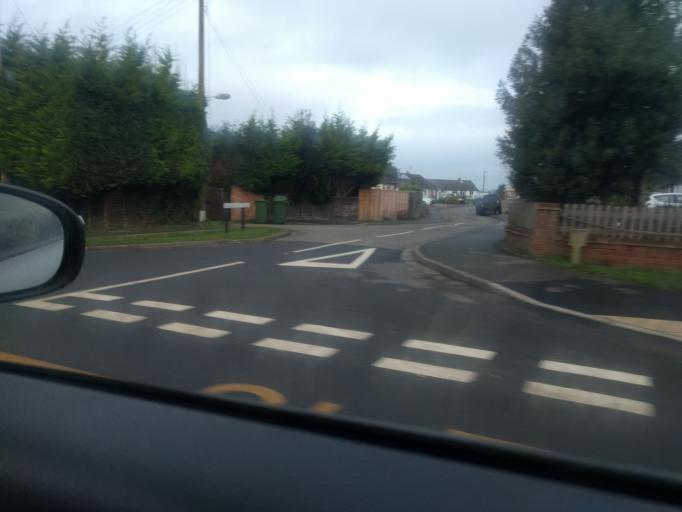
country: GB
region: England
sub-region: Gloucestershire
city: Mickleton
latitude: 52.1227
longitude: -1.7432
